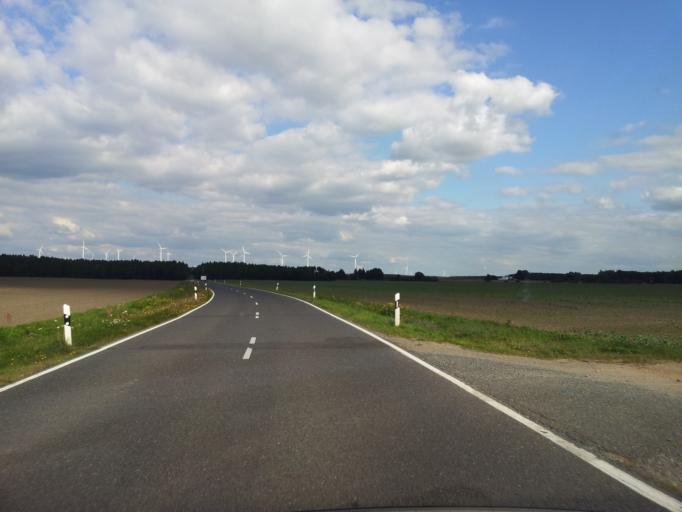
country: DE
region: Brandenburg
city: Sallgast
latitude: 51.6048
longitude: 13.7937
